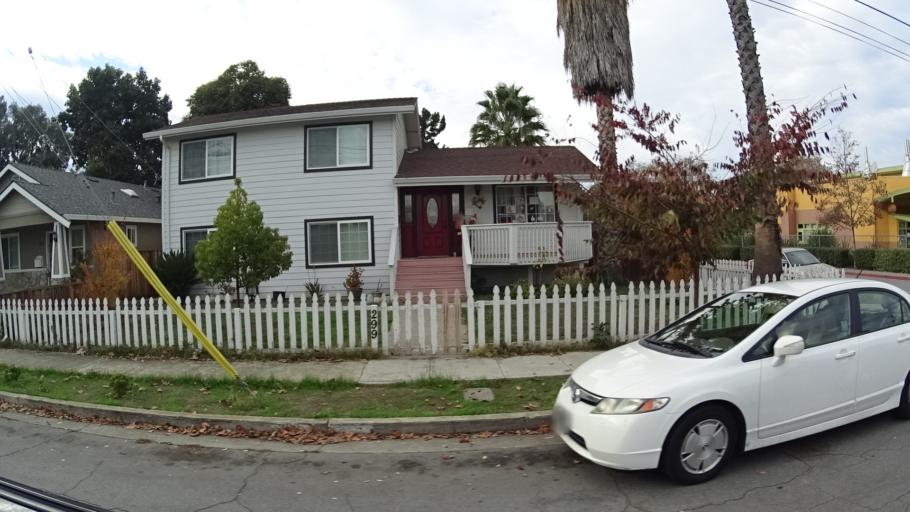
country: US
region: California
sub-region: Santa Clara County
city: Burbank
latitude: 37.3280
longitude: -121.9260
